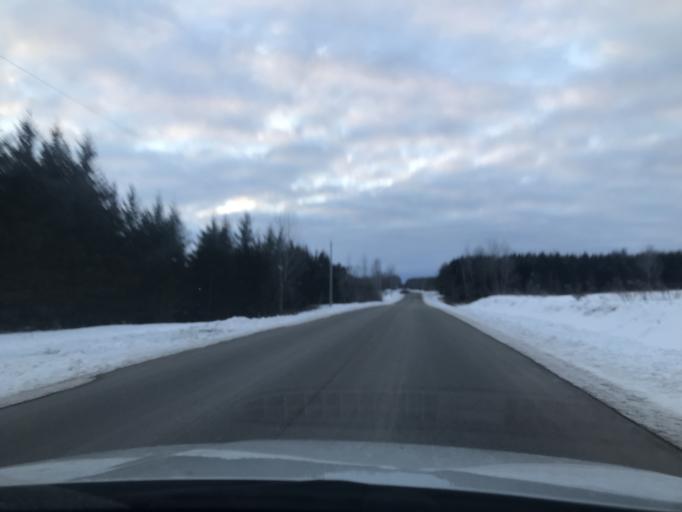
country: US
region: Wisconsin
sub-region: Marinette County
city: Peshtigo
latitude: 45.1647
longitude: -87.7564
